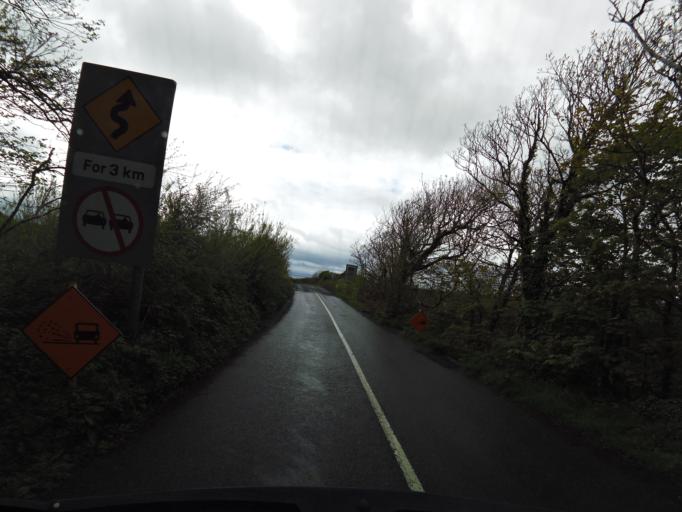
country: IE
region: Connaught
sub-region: County Galway
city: Bearna
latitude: 53.0467
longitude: -9.3416
